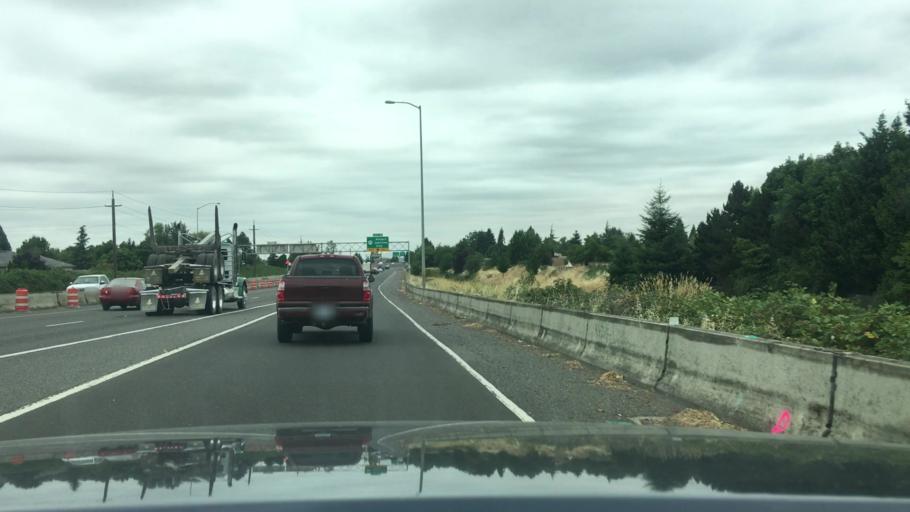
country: US
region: Oregon
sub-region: Lane County
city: Eugene
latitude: 44.0874
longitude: -123.1714
